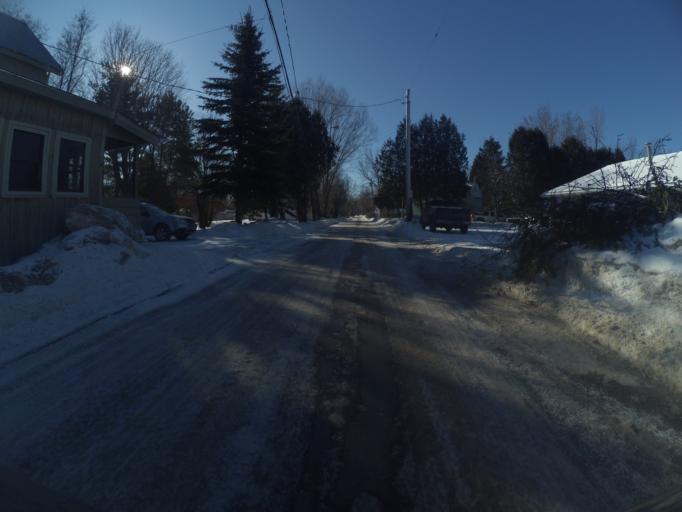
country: US
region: New York
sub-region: St. Lawrence County
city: Potsdam
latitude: 44.6773
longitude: -74.9927
